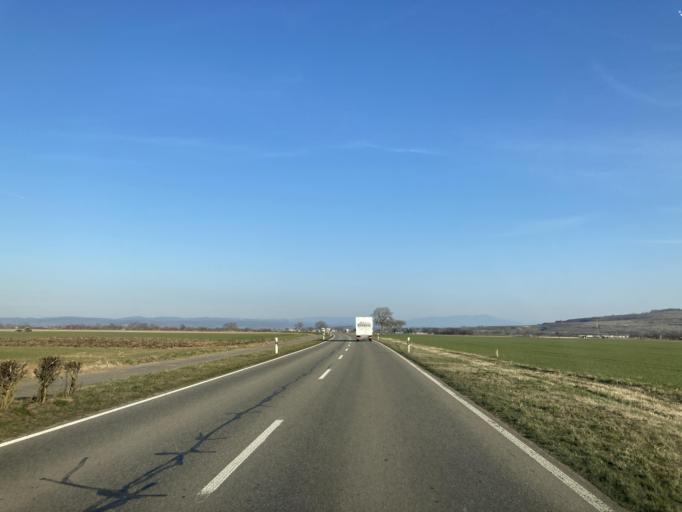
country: DE
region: Baden-Wuerttemberg
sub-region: Freiburg Region
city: Wyhl
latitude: 48.1501
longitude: 7.6448
